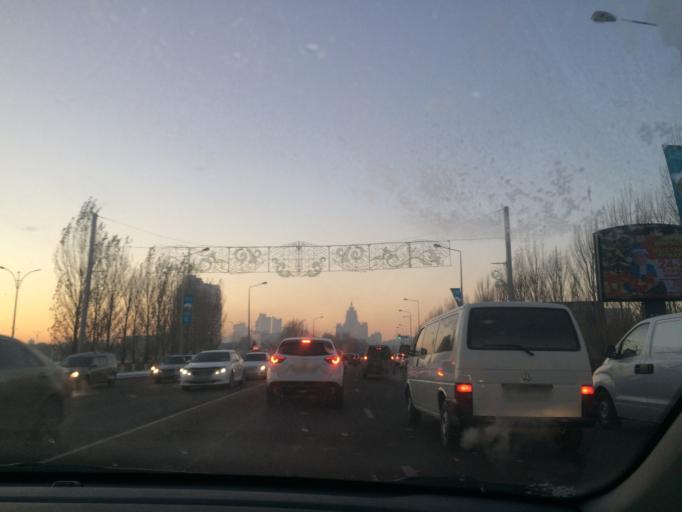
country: KZ
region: Astana Qalasy
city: Astana
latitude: 51.1543
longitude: 71.4123
